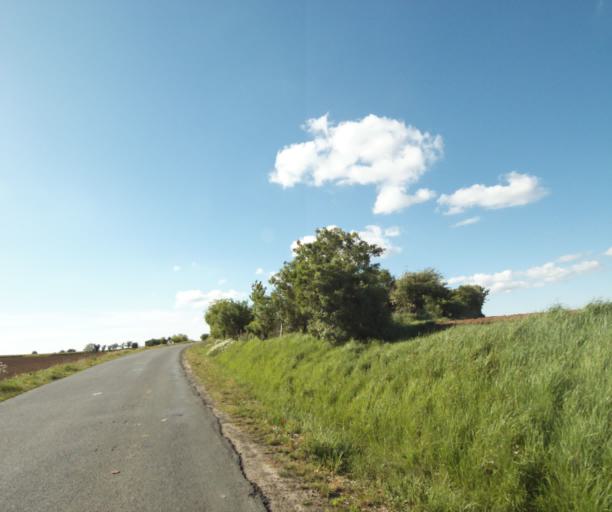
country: FR
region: Poitou-Charentes
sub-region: Departement de la Charente-Maritime
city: Corme-Royal
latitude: 45.7169
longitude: -0.8150
